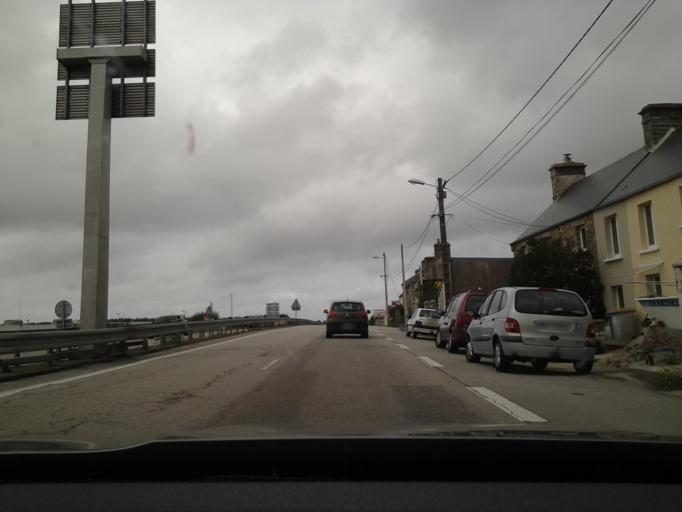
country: FR
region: Lower Normandy
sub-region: Departement de la Manche
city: La Glacerie
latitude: 49.6016
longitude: -1.5978
